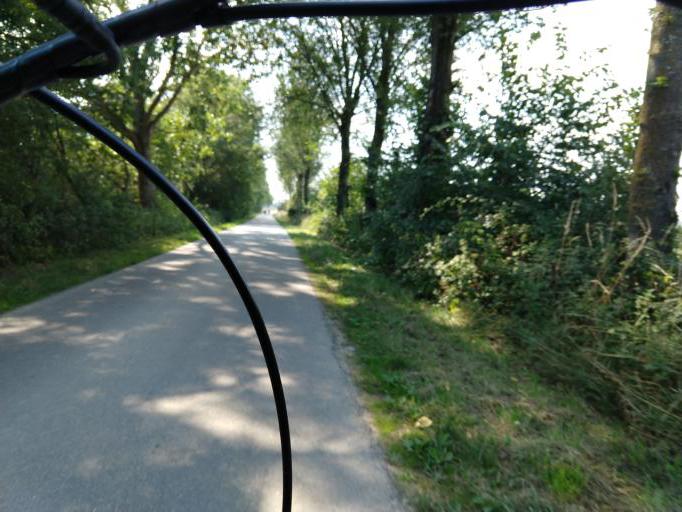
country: NL
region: Zeeland
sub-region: Gemeente Goes
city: Goes
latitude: 51.4494
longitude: 3.8701
